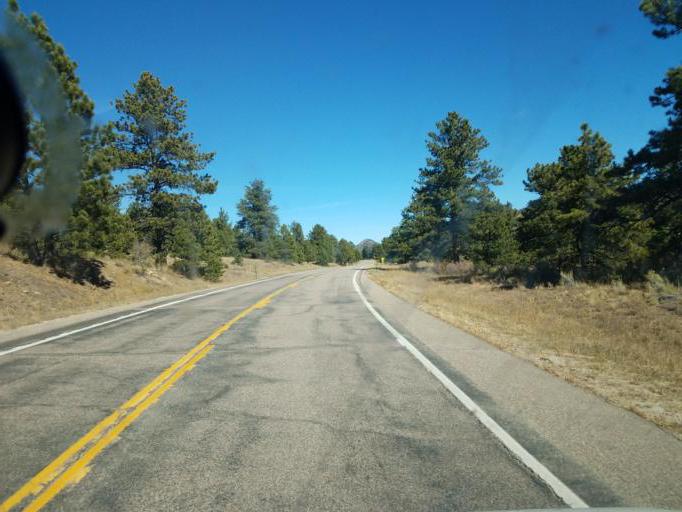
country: US
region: Colorado
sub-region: Custer County
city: Westcliffe
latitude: 38.1453
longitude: -105.3516
